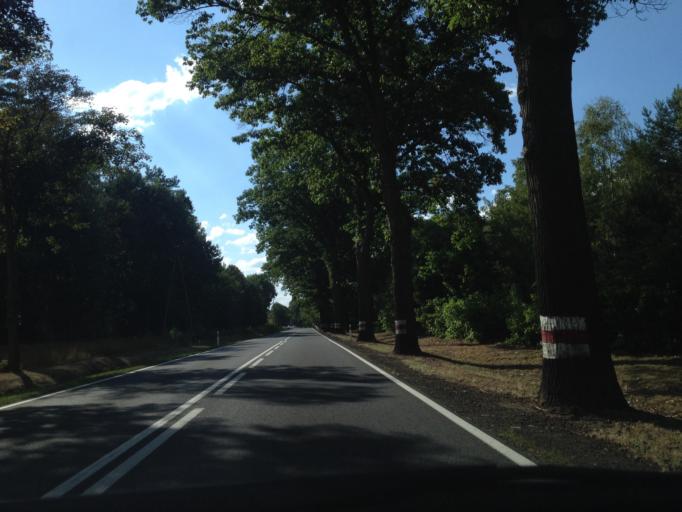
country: PL
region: Lubusz
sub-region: Powiat zarski
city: Lipinki Luzyckie
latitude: 51.6356
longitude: 14.9253
